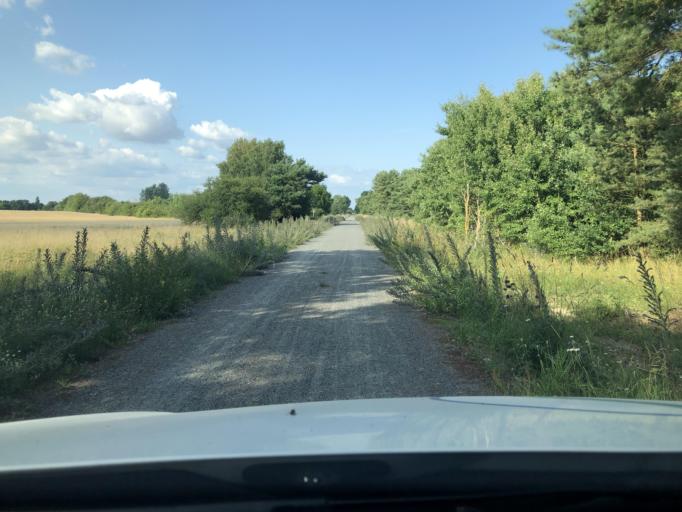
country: SE
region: Skane
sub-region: Kristianstads Kommun
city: Norra Asum
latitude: 55.9359
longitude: 14.1384
